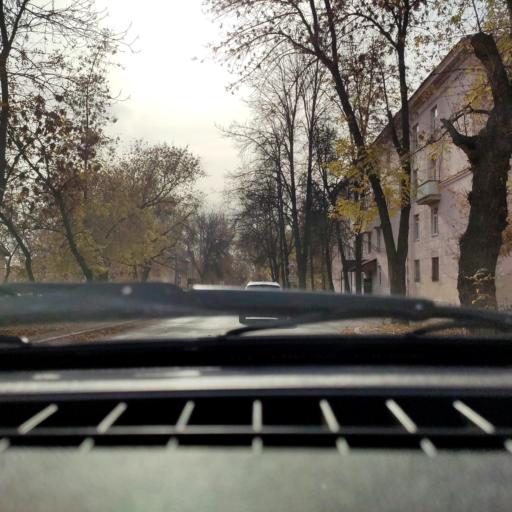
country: RU
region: Bashkortostan
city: Ufa
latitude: 54.8152
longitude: 56.0982
